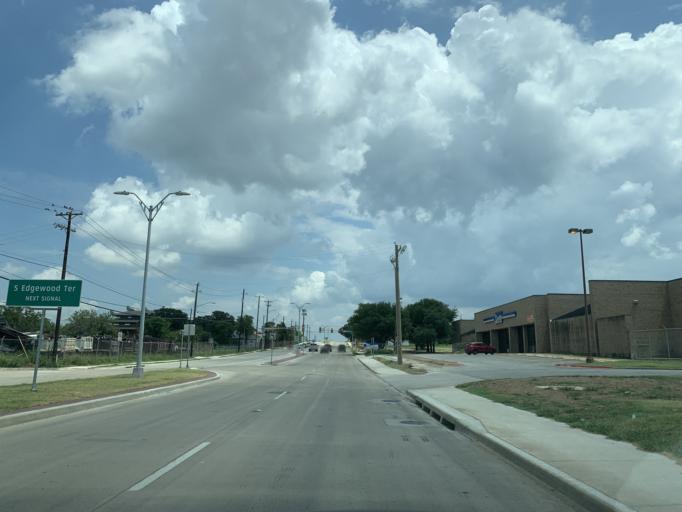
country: US
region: Texas
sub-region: Tarrant County
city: Forest Hill
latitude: 32.7311
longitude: -97.2555
